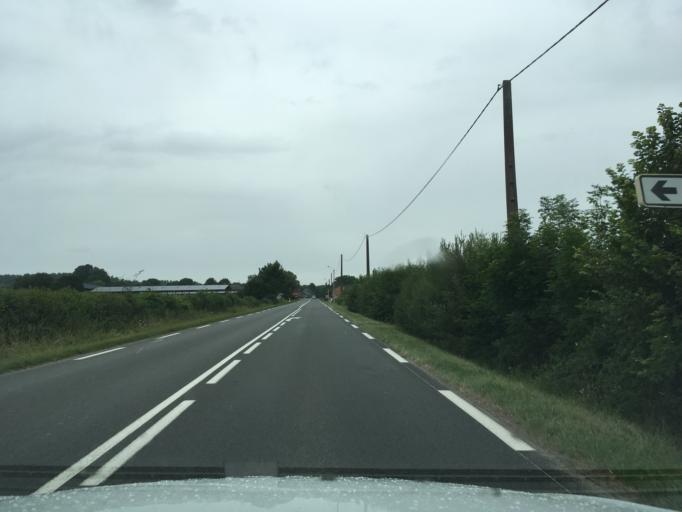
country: FR
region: Picardie
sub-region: Departement de l'Aisne
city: Buironfosse
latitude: 49.9567
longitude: 3.8094
